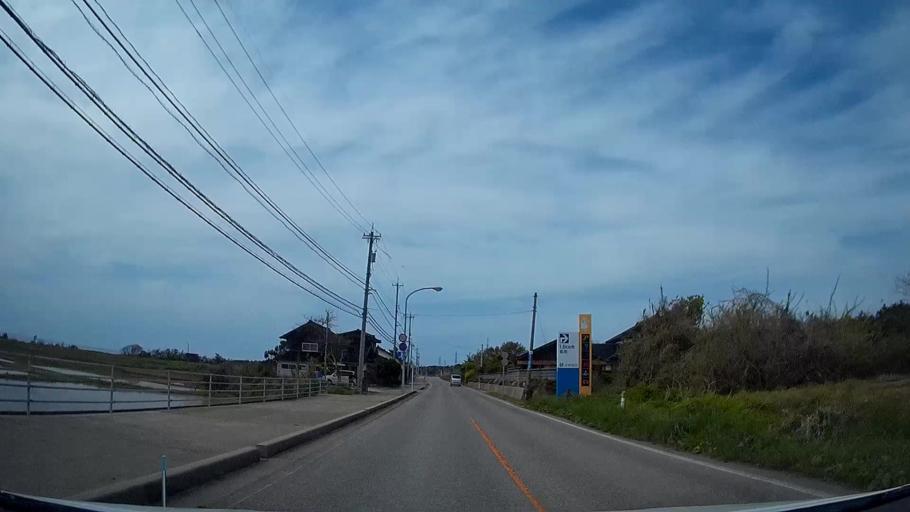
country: JP
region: Ishikawa
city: Hakui
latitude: 37.0428
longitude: 136.7401
